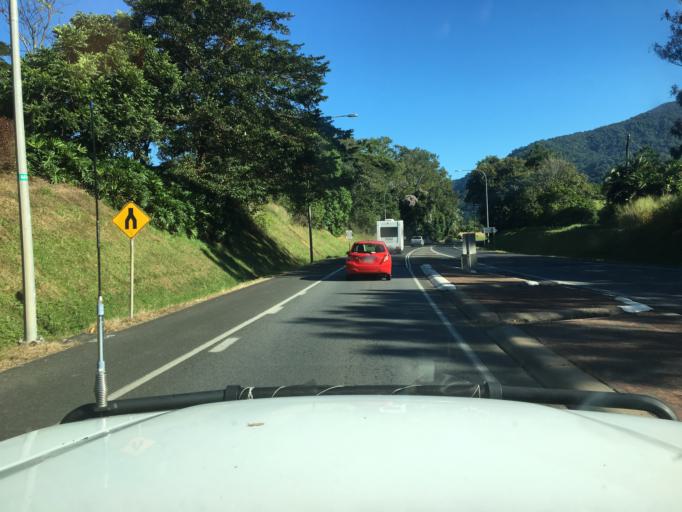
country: AU
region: Queensland
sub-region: Cairns
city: Redlynch
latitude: -16.8792
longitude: 145.6883
